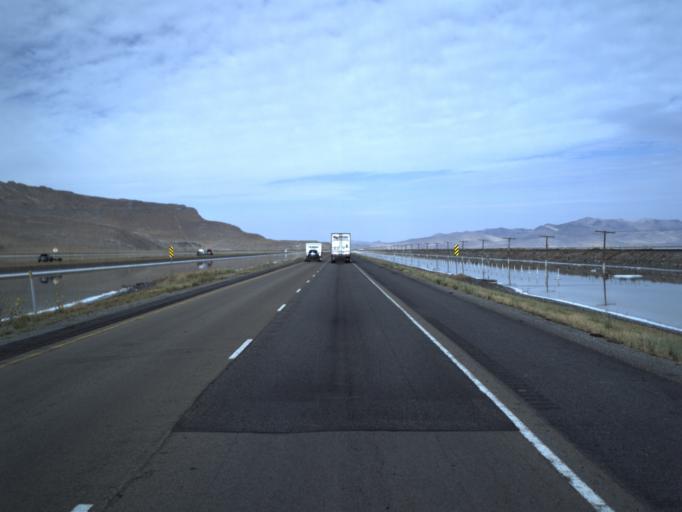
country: US
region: Utah
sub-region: Tooele County
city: Grantsville
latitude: 40.7308
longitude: -112.5897
